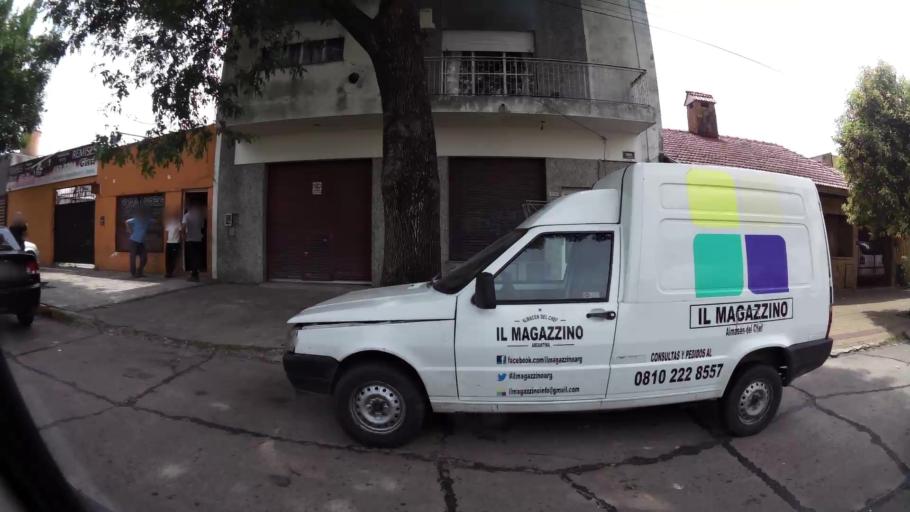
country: AR
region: Buenos Aires
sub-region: Partido de La Plata
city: La Plata
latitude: -34.9482
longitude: -57.9592
